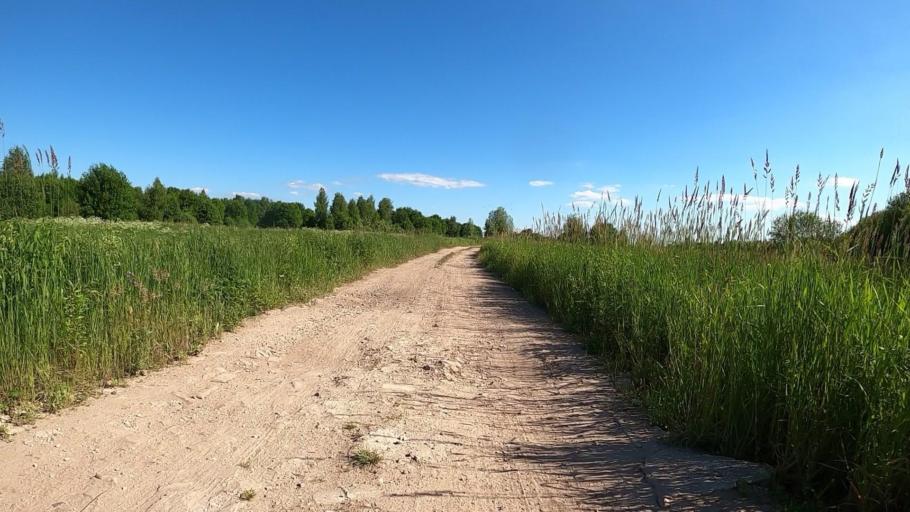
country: LV
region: Stopini
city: Ulbroka
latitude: 56.8978
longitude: 24.3160
